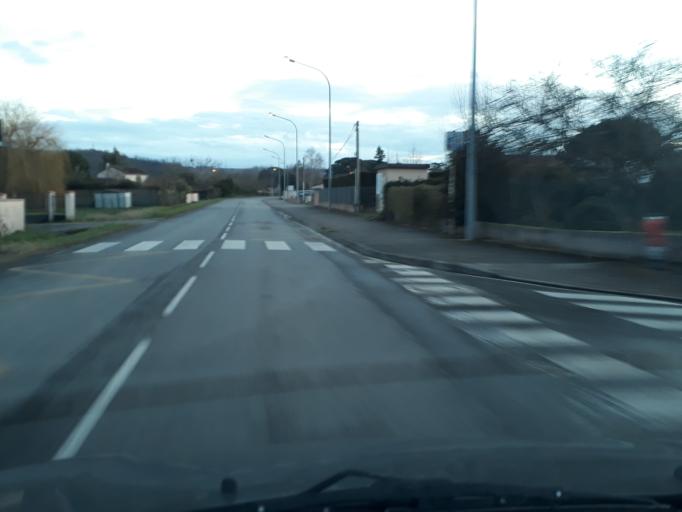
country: FR
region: Midi-Pyrenees
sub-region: Departement de la Haute-Garonne
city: Carbonne
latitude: 43.3069
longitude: 1.2295
